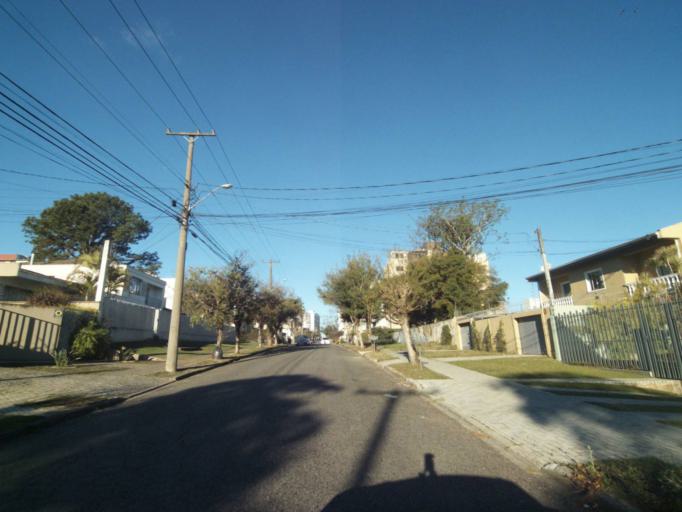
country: BR
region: Parana
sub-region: Curitiba
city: Curitiba
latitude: -25.4623
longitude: -49.2949
